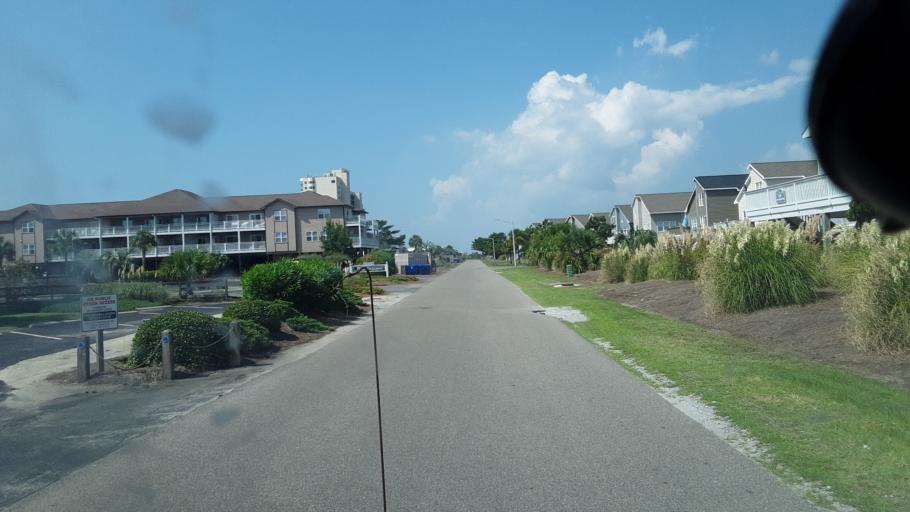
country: US
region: North Carolina
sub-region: Brunswick County
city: Sunset Beach
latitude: 33.8800
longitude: -78.4668
